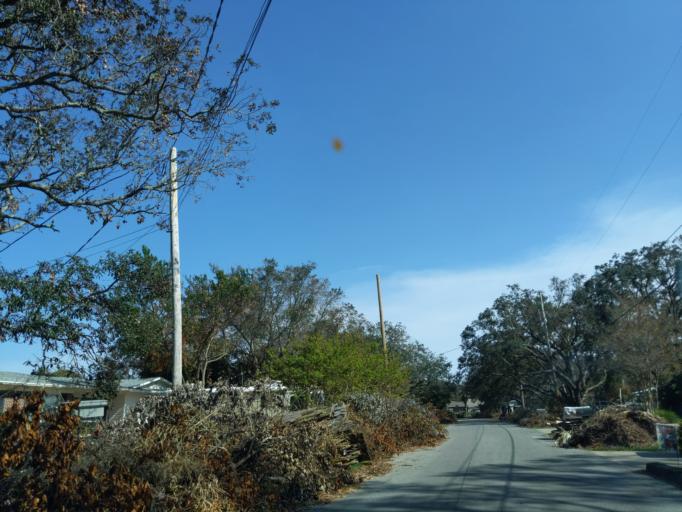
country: US
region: Florida
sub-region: Santa Rosa County
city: Gulf Breeze
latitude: 30.3546
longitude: -87.1889
